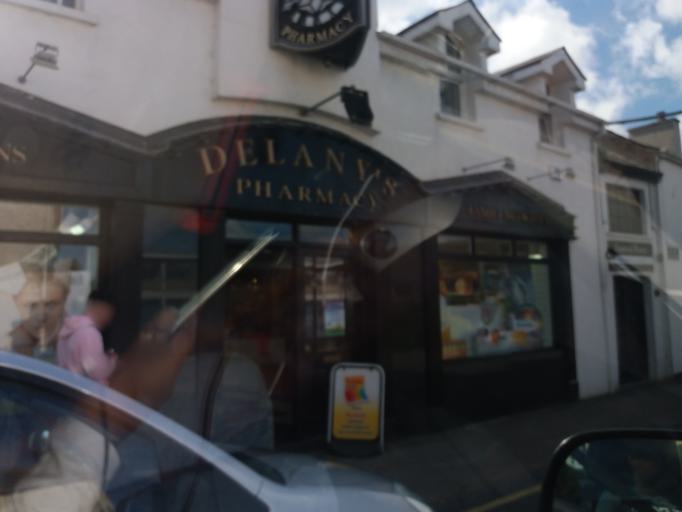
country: IE
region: Munster
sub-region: Waterford
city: Waterford
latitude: 52.2546
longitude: -7.1092
